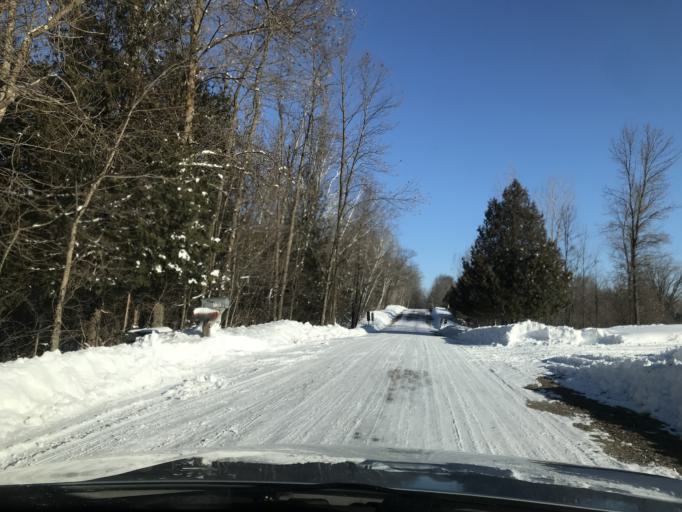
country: US
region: Wisconsin
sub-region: Oconto County
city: Oconto
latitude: 44.9532
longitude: -87.9770
